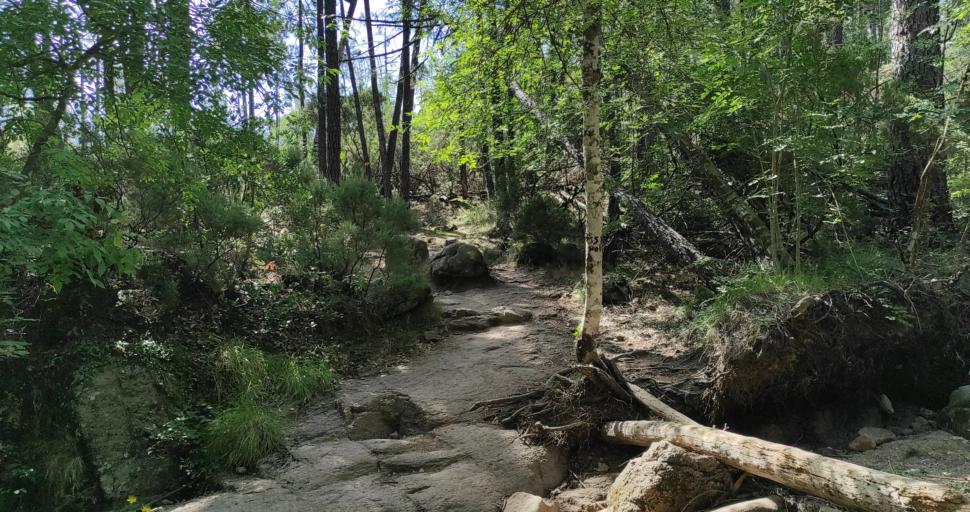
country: FR
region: Corsica
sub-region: Departement de la Corse-du-Sud
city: Zonza
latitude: 41.6843
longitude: 9.2030
